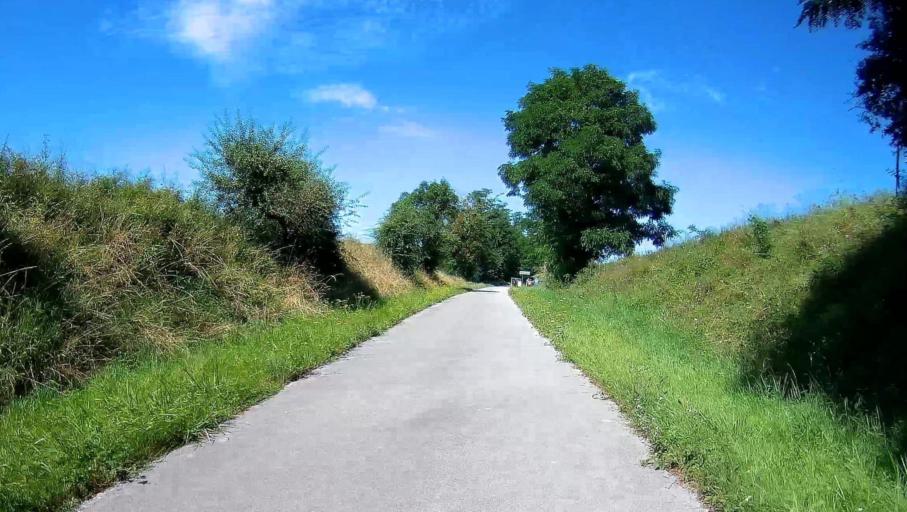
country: FR
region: Bourgogne
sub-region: Departement de la Cote-d'Or
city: Nolay
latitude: 46.9010
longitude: 4.6724
